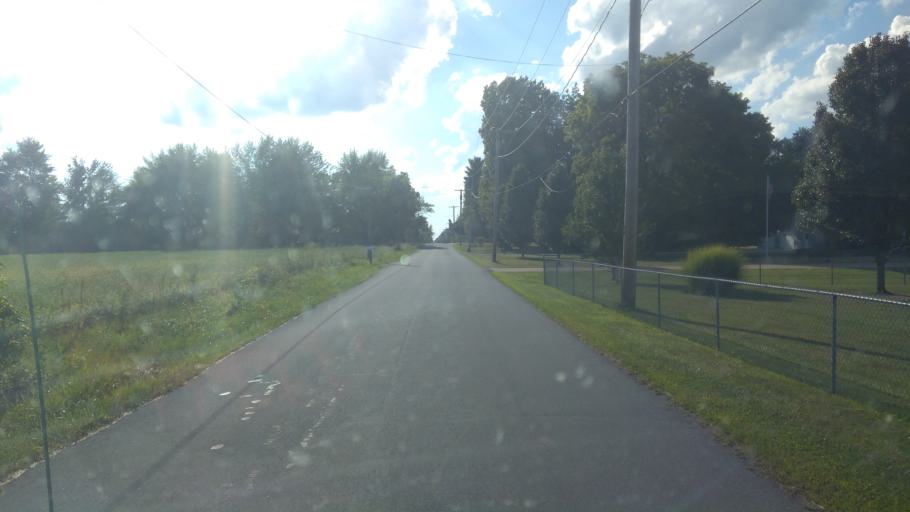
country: US
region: Ohio
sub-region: Crawford County
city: Galion
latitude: 40.7556
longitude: -82.7756
